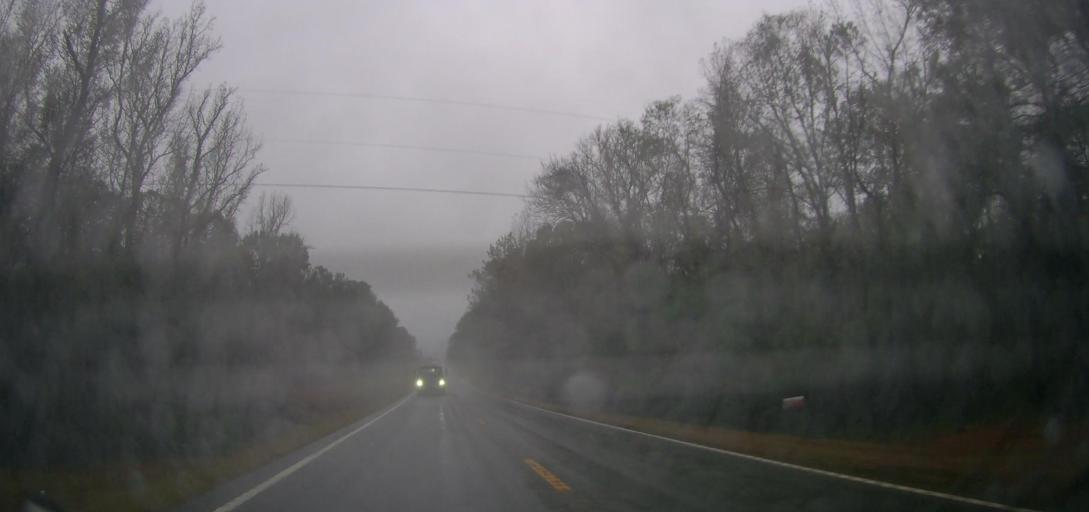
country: US
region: Georgia
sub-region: Jones County
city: Gray
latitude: 33.1200
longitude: -83.4771
